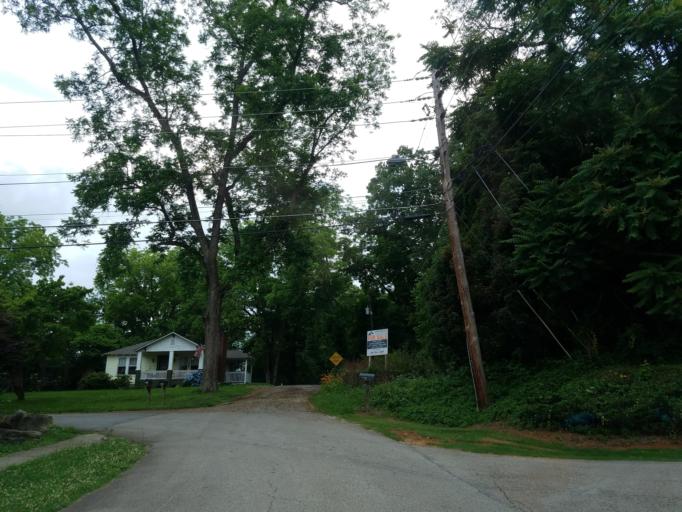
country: US
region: Georgia
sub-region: Lumpkin County
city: Dahlonega
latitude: 34.5327
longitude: -83.9875
